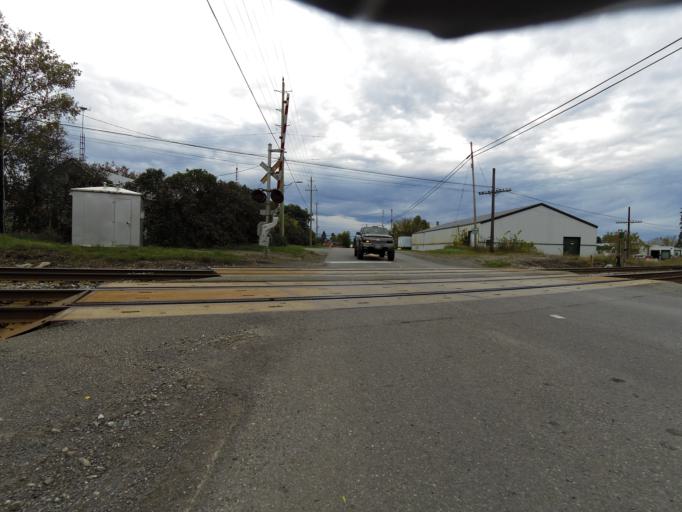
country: CA
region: Ontario
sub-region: Lanark County
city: Smiths Falls
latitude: 44.9213
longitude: -75.8385
